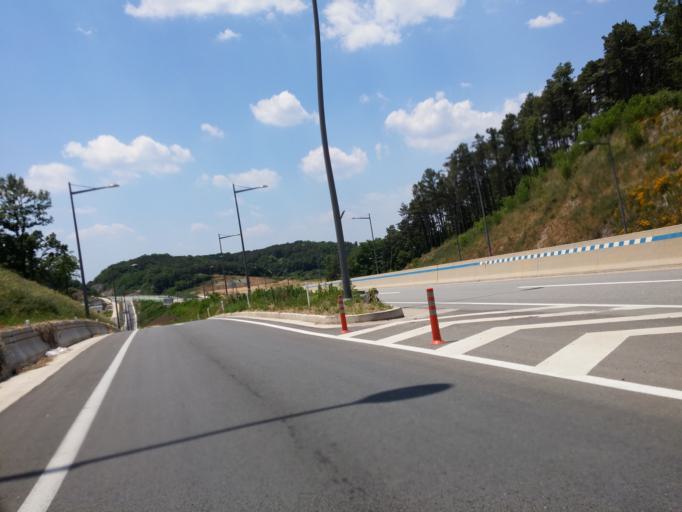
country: KR
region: Chungcheongbuk-do
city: Cheongju-si
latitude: 36.6014
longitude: 127.4436
